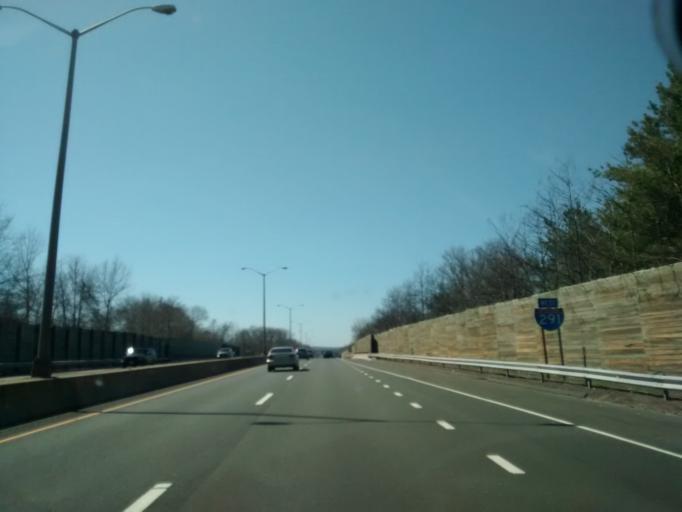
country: US
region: Connecticut
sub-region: Hartford County
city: South Windsor
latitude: 41.8078
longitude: -72.6236
